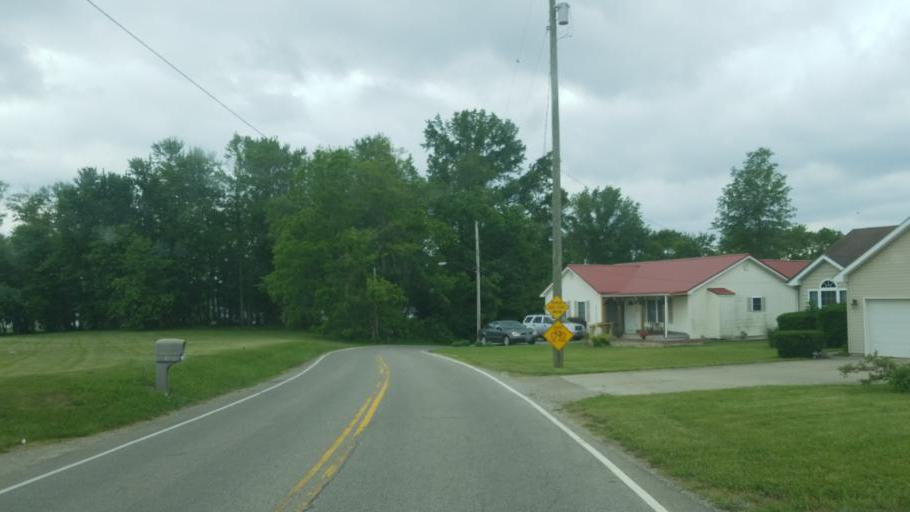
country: US
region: Ohio
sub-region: Fairfield County
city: Baltimore
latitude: 39.8493
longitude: -82.5968
